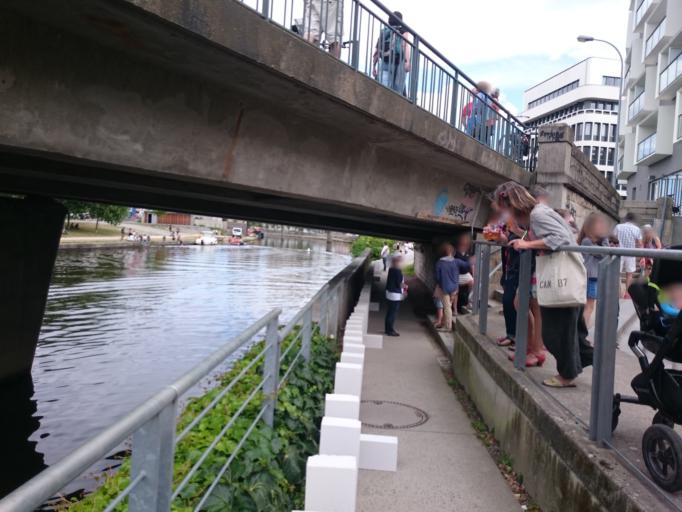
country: FR
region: Brittany
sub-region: Departement d'Ille-et-Vilaine
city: Rennes
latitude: 48.1077
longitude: -1.6950
